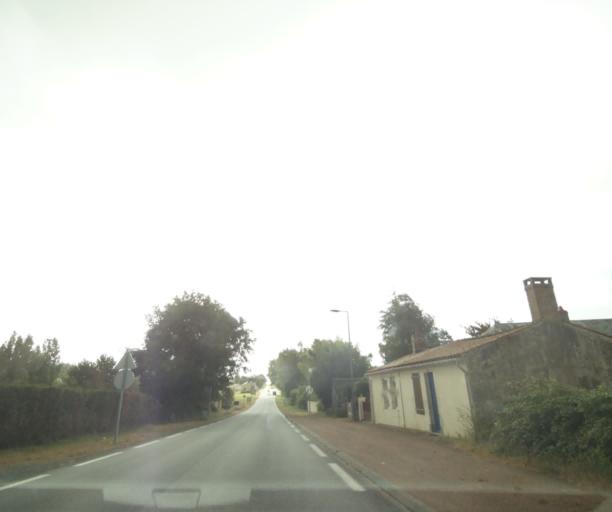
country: FR
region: Pays de la Loire
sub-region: Departement de la Vendee
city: Avrille
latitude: 46.4693
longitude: -1.4873
